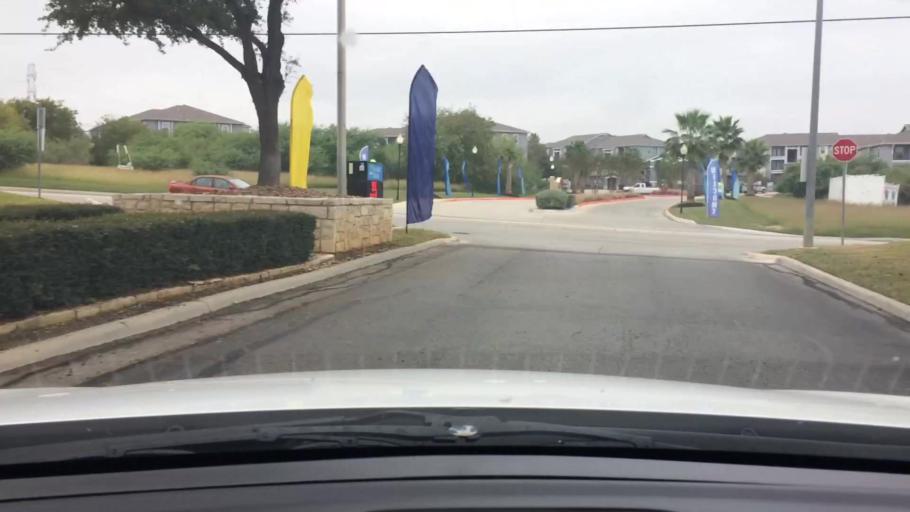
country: US
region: Texas
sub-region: Bexar County
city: Converse
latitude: 29.5245
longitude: -98.3420
